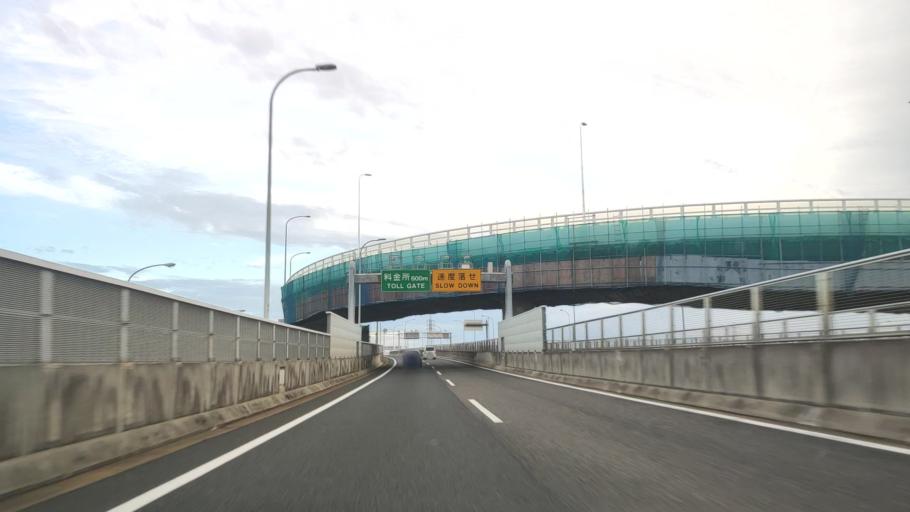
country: JP
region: Aichi
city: Nagoya-shi
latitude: 35.2315
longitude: 136.9098
